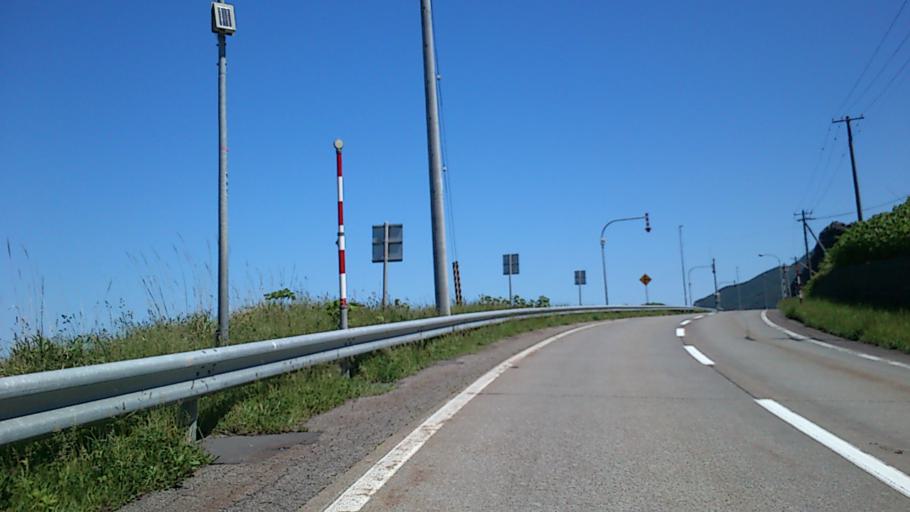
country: JP
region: Hokkaido
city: Rumoi
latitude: 43.7529
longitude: 141.3499
